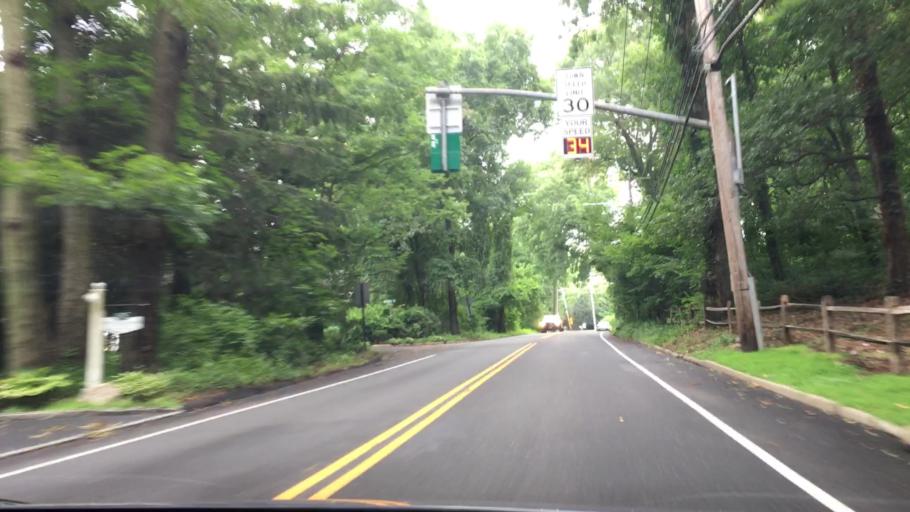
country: US
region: New York
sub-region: Suffolk County
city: West Hills
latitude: 40.8071
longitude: -73.4422
